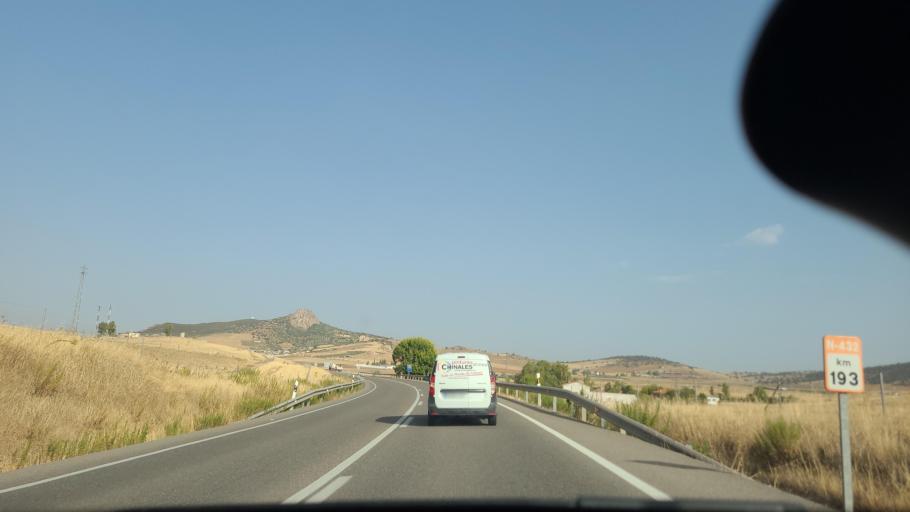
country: ES
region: Andalusia
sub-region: Province of Cordoba
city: Penarroya-Pueblonuevo
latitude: 38.3054
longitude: -5.2580
